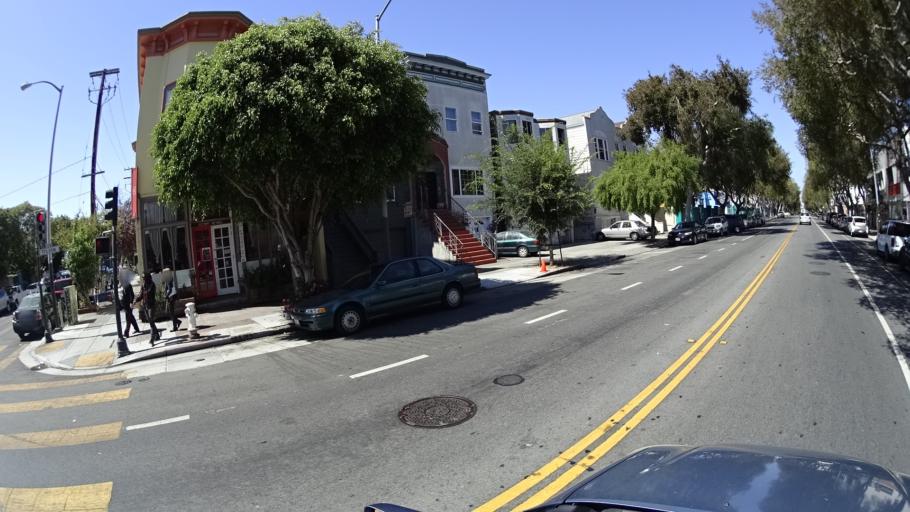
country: US
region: California
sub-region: San Francisco County
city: San Francisco
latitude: 37.7541
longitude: -122.4142
